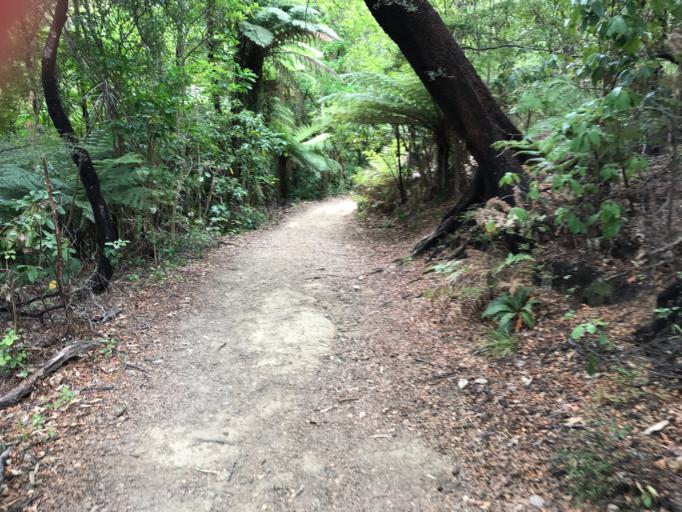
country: NZ
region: Marlborough
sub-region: Marlborough District
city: Picton
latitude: -41.0988
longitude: 174.1862
